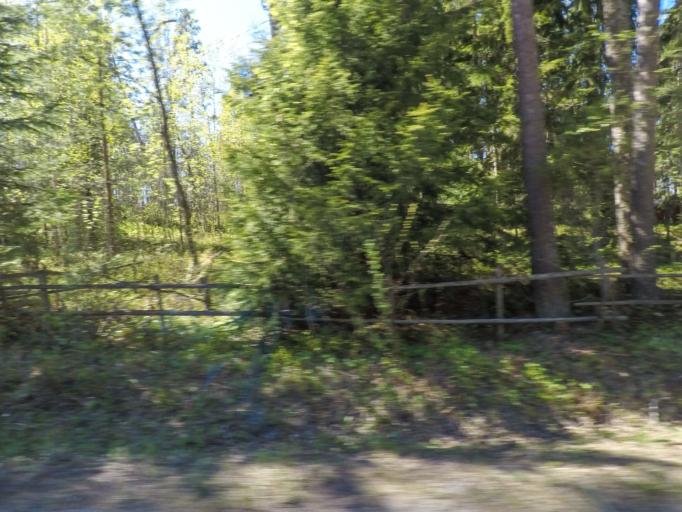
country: FI
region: Uusimaa
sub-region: Helsinki
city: Sammatti
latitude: 60.3384
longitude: 23.8011
